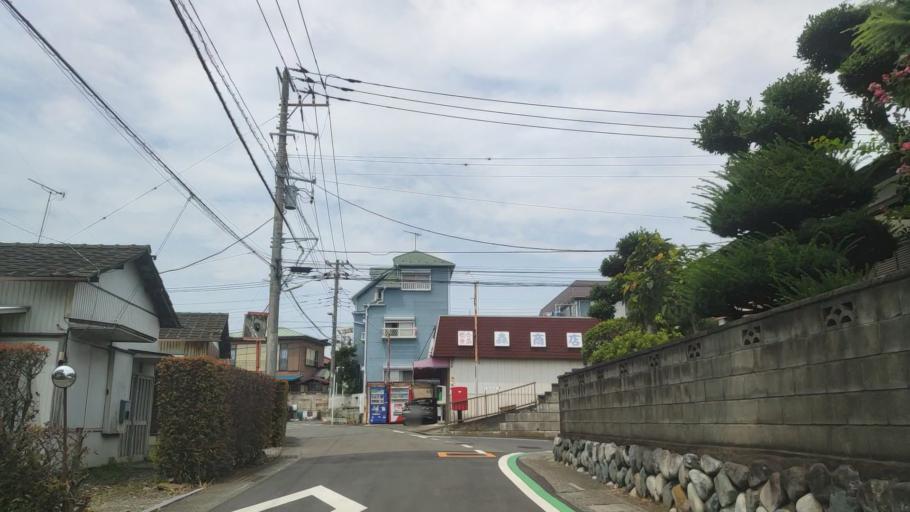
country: JP
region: Kanagawa
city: Atsugi
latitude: 35.4333
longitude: 139.3950
